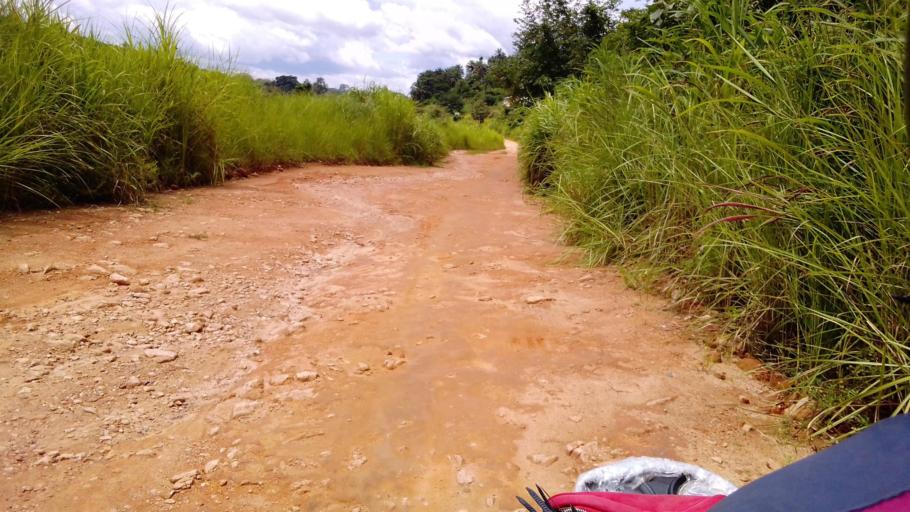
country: SL
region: Eastern Province
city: Koyima
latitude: 8.6889
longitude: -11.0078
